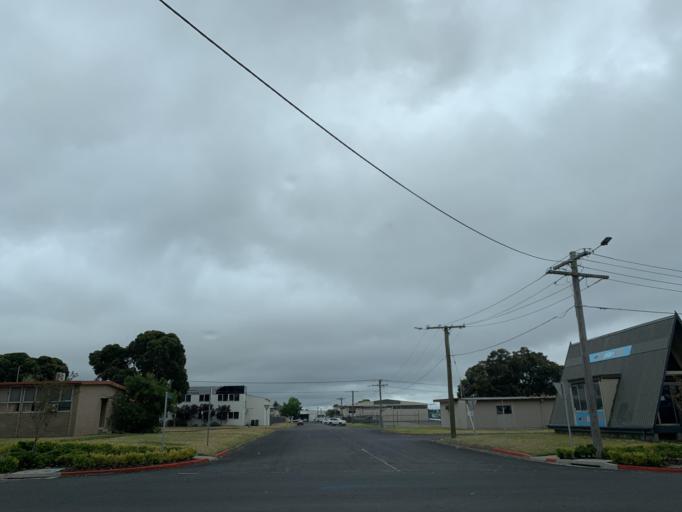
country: AU
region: Victoria
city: Heatherton
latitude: -37.9764
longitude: 145.0923
